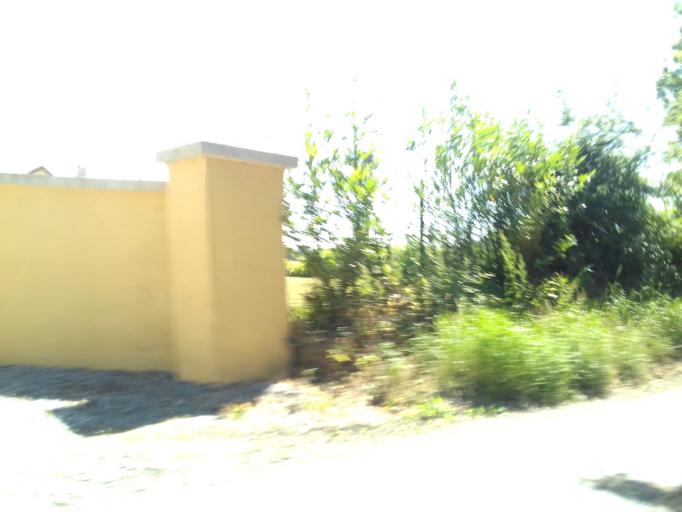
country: IE
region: Leinster
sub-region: Fingal County
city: Swords
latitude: 53.5069
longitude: -6.2675
